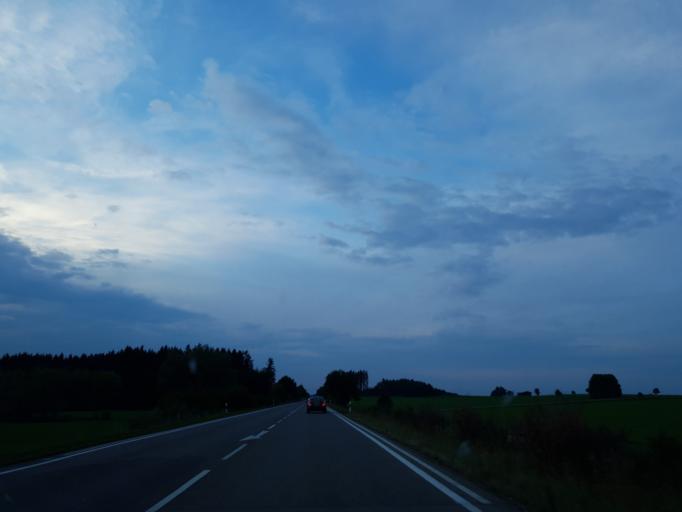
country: DE
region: Bavaria
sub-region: Swabia
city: Mauerstetten
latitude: 47.8509
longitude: 10.6664
